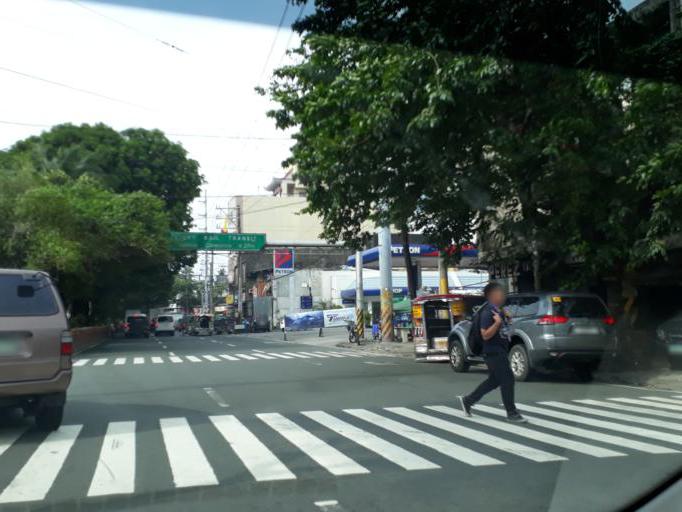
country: PH
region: Metro Manila
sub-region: City of Manila
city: Manila
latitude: 14.6303
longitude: 120.9801
